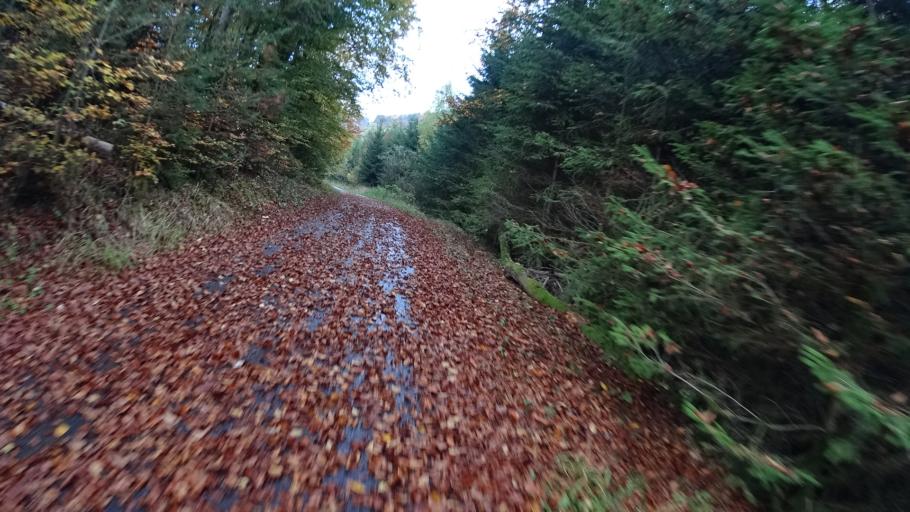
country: DE
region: Bavaria
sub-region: Upper Bavaria
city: Adelschlag
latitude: 48.8469
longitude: 11.2593
